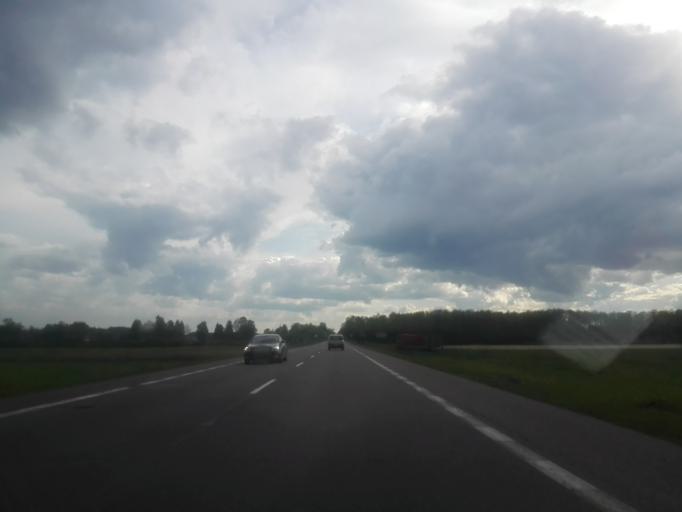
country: PL
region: Podlasie
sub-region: Powiat zambrowski
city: Szumowo
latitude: 52.8781
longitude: 22.0352
